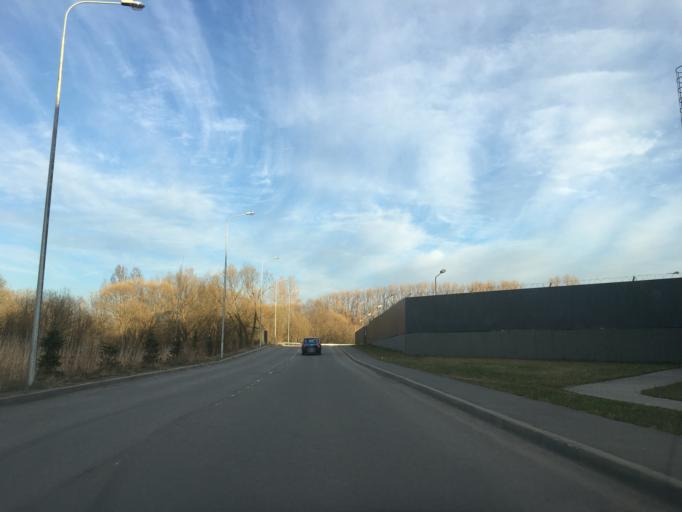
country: RU
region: St.-Petersburg
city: Uritsk
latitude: 59.8443
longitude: 30.1810
